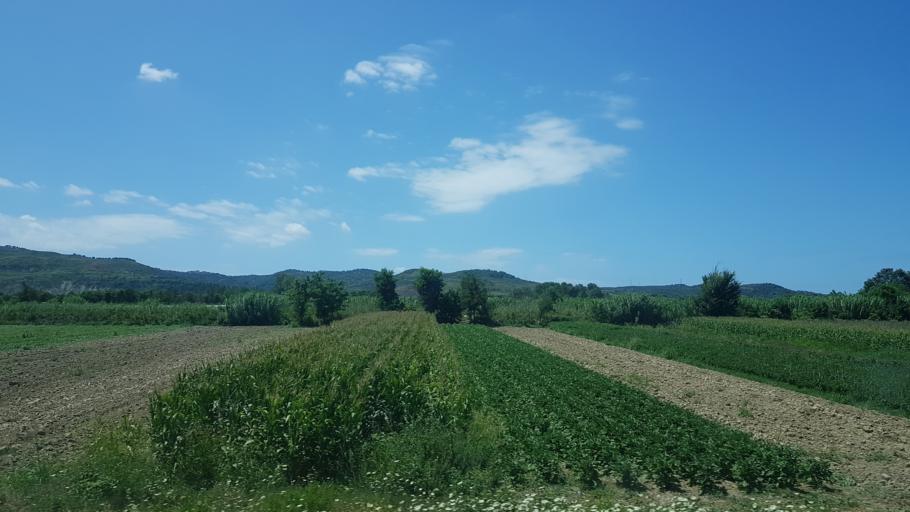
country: AL
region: Fier
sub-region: Rrethi i Fierit
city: Frakulla e Madhe
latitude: 40.6117
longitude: 19.5252
